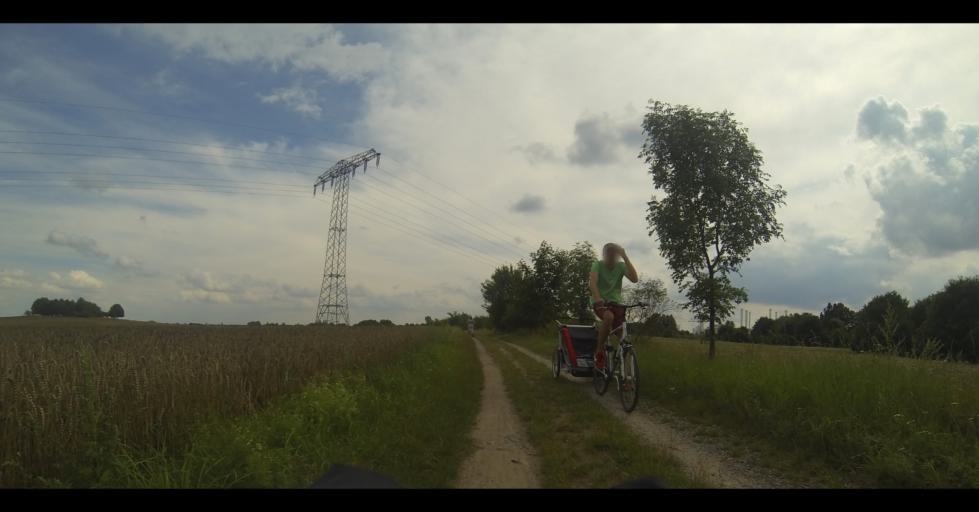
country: DE
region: Saxony
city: Moritzburg
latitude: 51.1321
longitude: 13.7147
